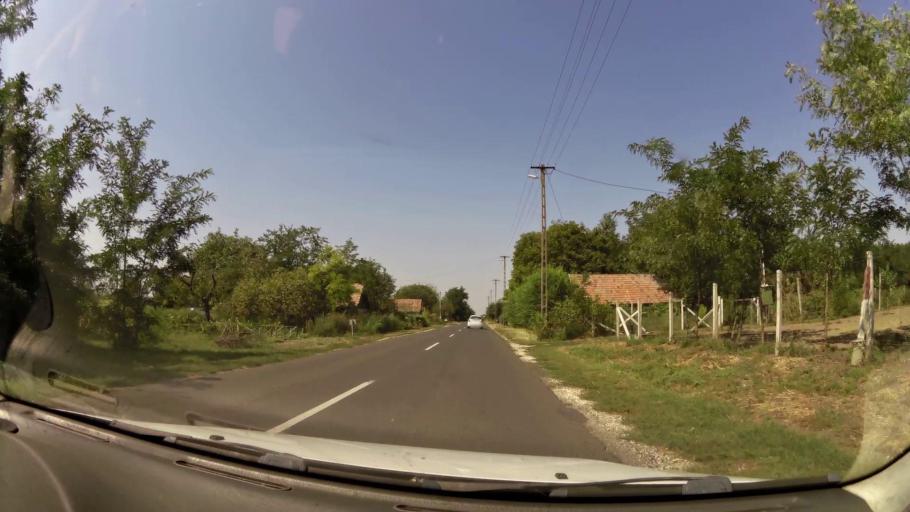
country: HU
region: Pest
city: Tapioszentmarton
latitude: 47.3449
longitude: 19.7262
